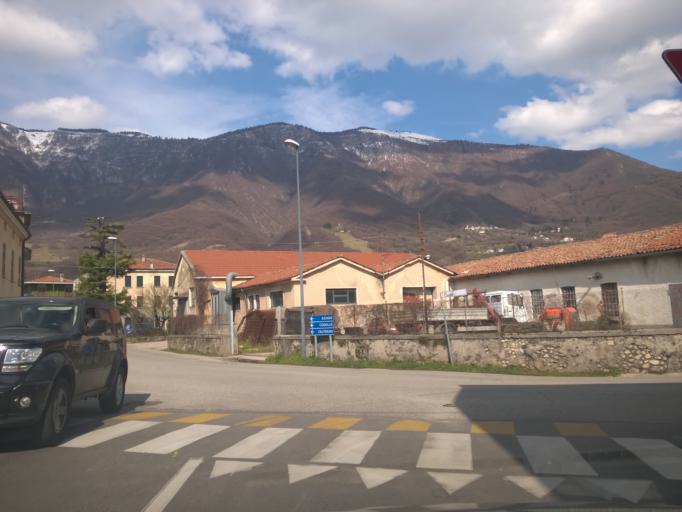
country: IT
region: Veneto
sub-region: Provincia di Vicenza
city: Chiuppano
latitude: 45.7664
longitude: 11.4587
